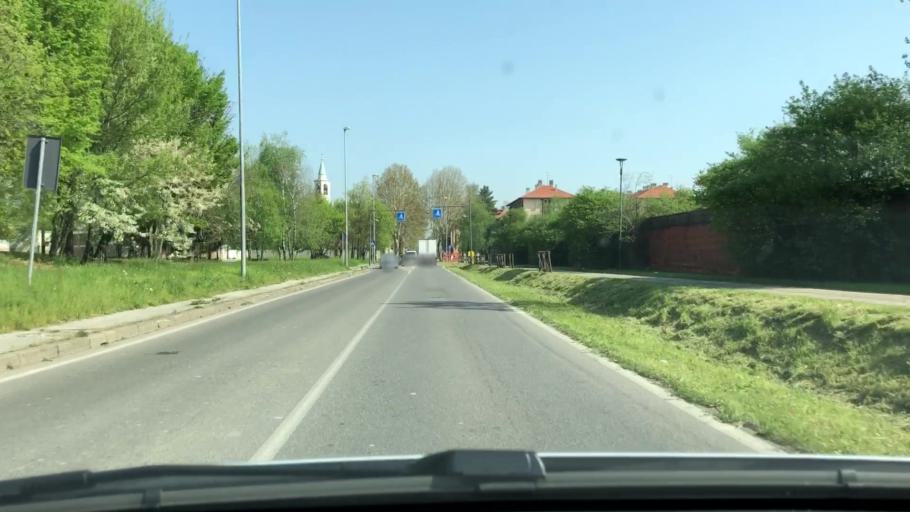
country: IT
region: Lombardy
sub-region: Provincia di Monza e Brianza
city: Barlassina
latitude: 45.6357
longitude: 9.1198
